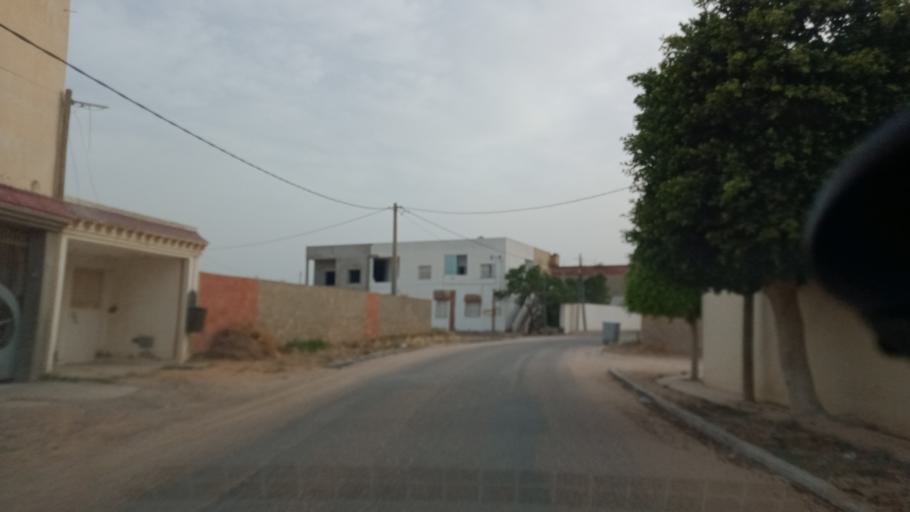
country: TN
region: Safaqis
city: Al Qarmadah
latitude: 34.7852
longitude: 10.7685
